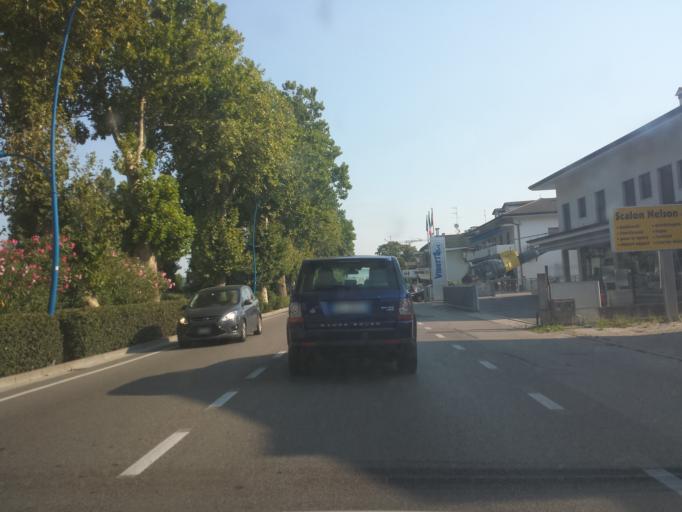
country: IT
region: Veneto
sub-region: Provincia di Venezia
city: Iesolo
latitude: 45.5260
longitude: 12.6407
